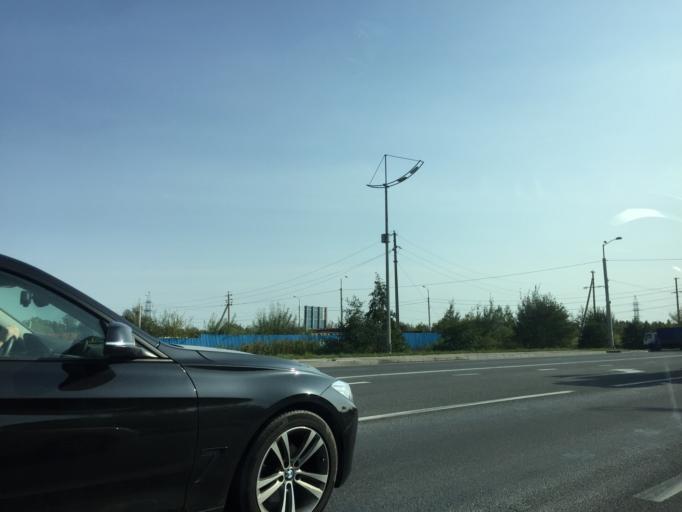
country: RU
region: Kaliningrad
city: Bol'shoe Isakovo
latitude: 54.6835
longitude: 20.5994
